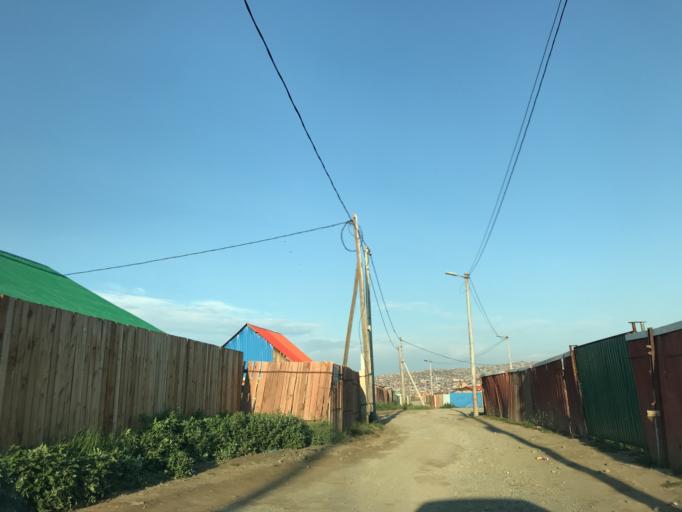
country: MN
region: Ulaanbaatar
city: Ulaanbaatar
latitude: 47.9526
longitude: 106.9430
